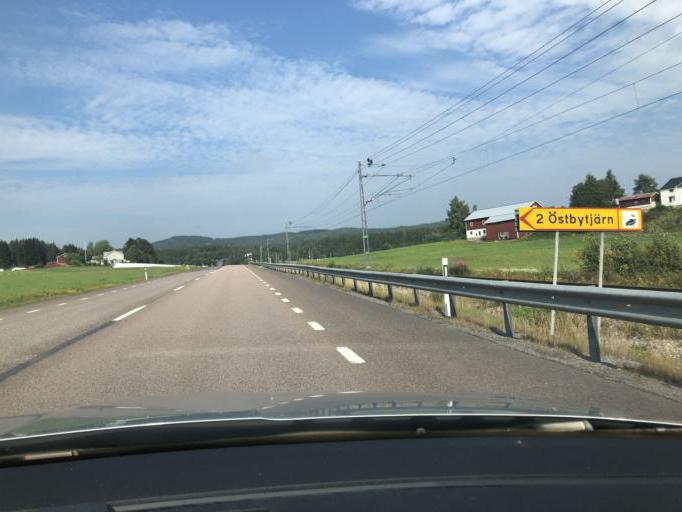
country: SE
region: Vaesternorrland
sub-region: Kramfors Kommun
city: Kramfors
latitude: 62.8221
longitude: 17.8494
